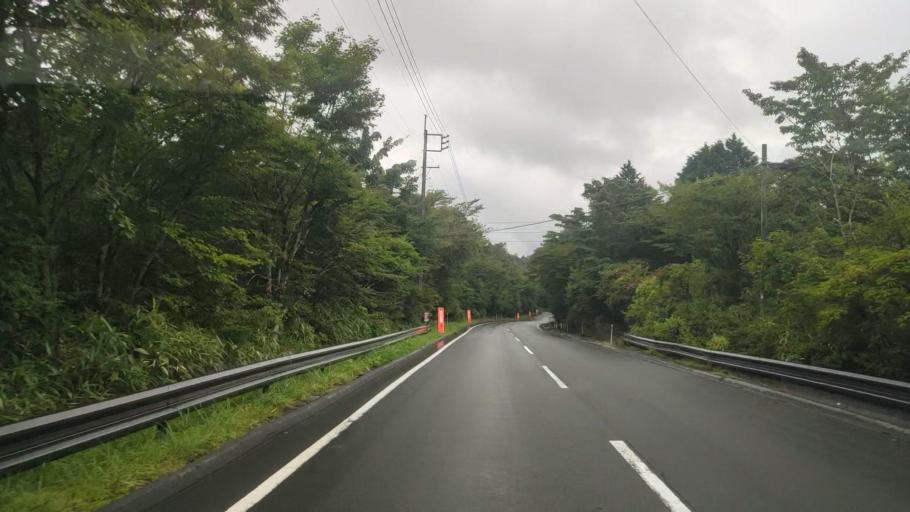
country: JP
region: Shizuoka
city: Fuji
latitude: 35.2814
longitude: 138.7810
